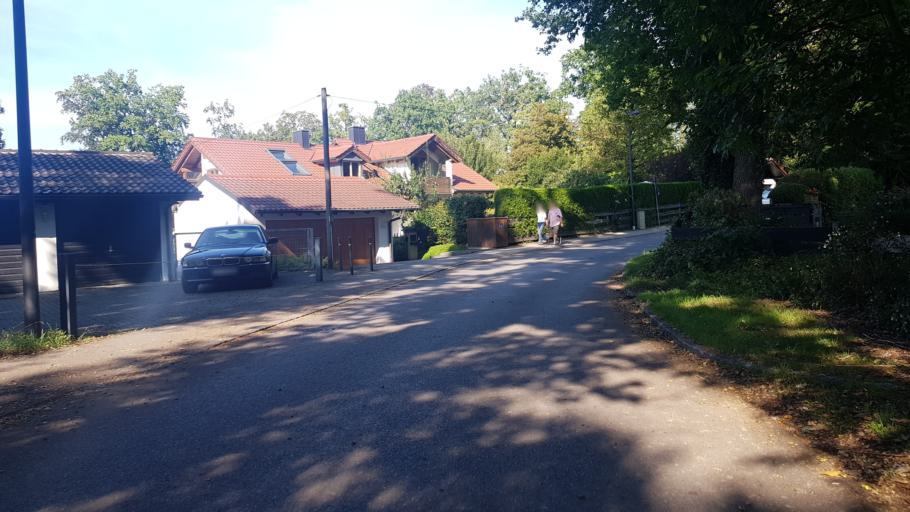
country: DE
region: Bavaria
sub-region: Upper Bavaria
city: Wessling
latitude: 48.0698
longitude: 11.2493
